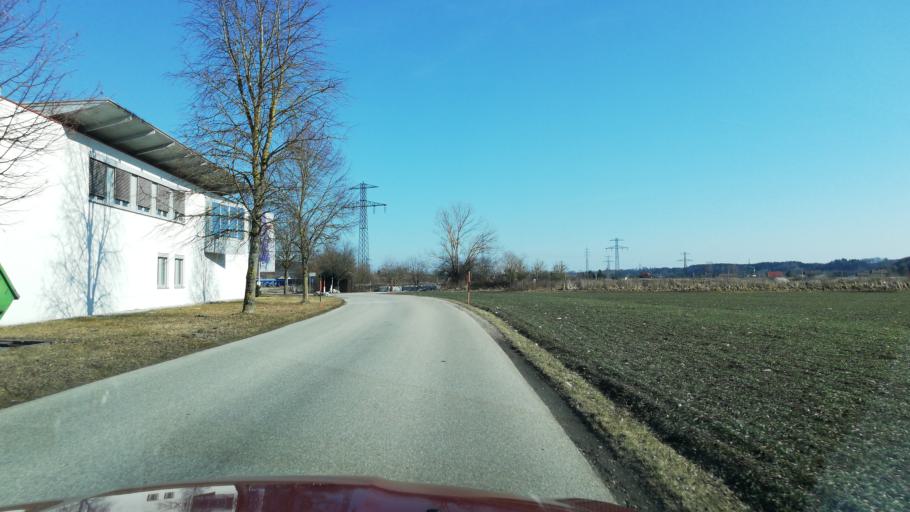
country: AT
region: Upper Austria
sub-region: Politischer Bezirk Vocklabruck
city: Aurach am Hongar
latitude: 47.9869
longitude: 13.6775
